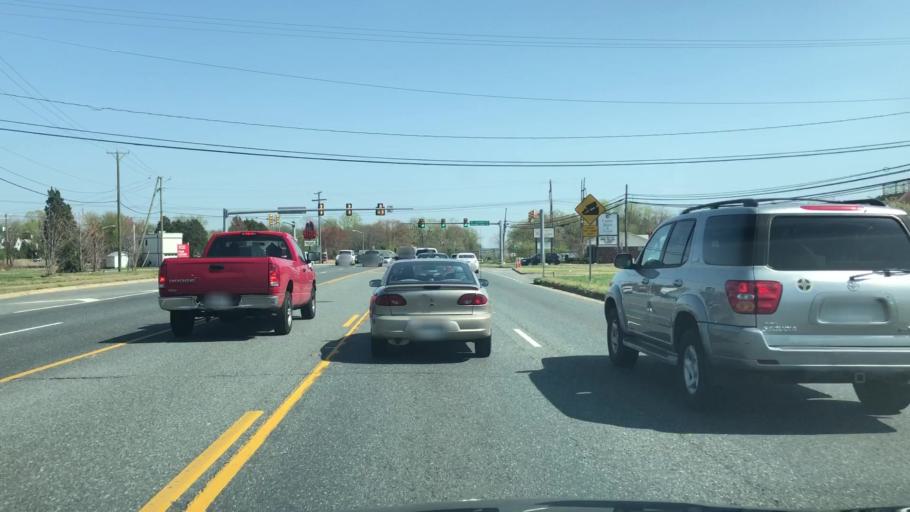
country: US
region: Virginia
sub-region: Stafford County
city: Falmouth
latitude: 38.3337
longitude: -77.4801
